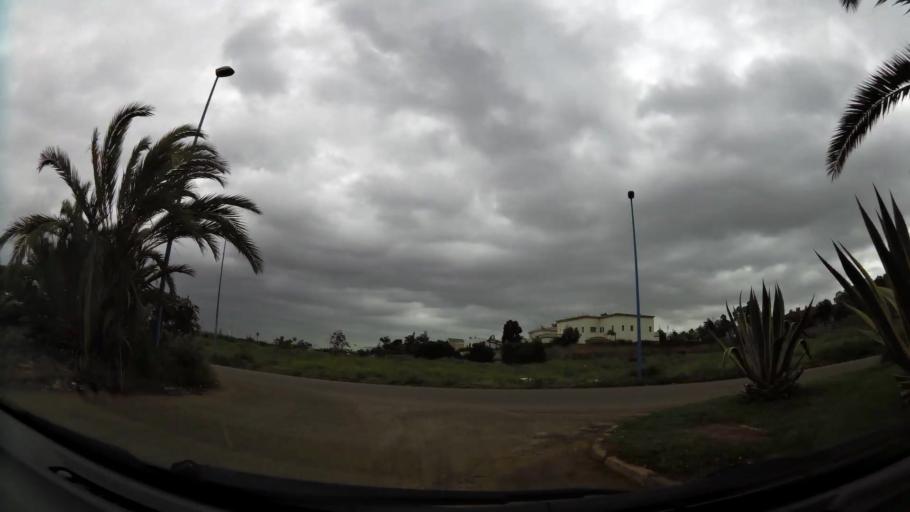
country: MA
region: Grand Casablanca
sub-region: Casablanca
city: Casablanca
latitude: 33.5397
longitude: -7.6346
